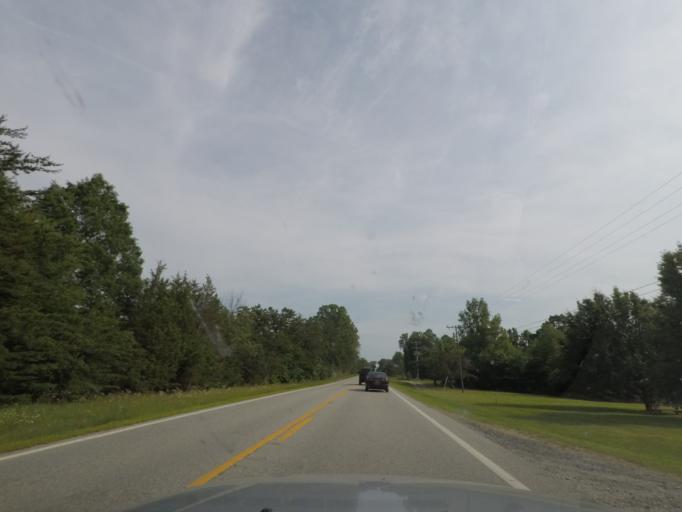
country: US
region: Virginia
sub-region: Prince Edward County
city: Hampden Sydney
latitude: 37.1952
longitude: -78.4299
